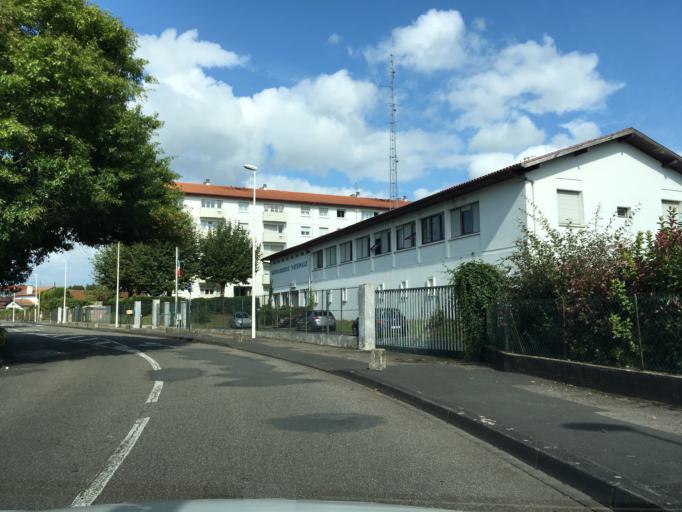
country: FR
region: Aquitaine
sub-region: Departement des Pyrenees-Atlantiques
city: Bayonne
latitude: 43.4764
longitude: -1.4829
